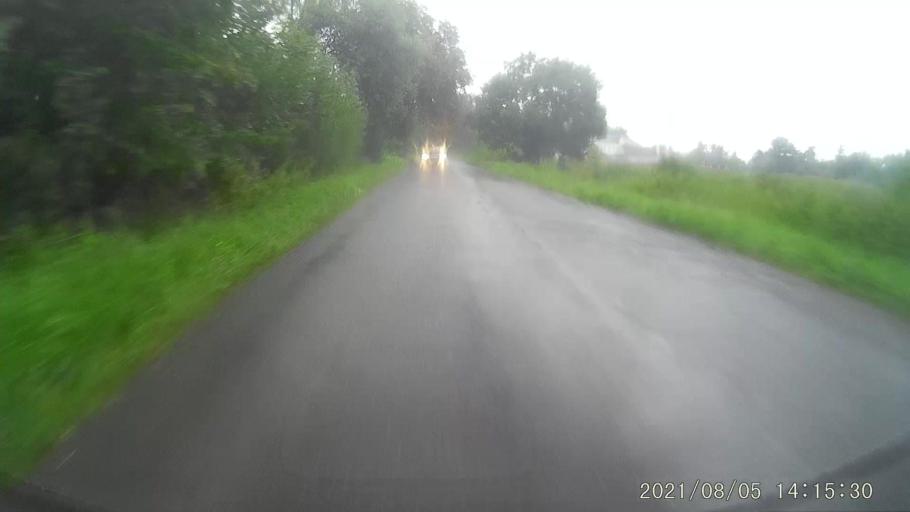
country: PL
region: Opole Voivodeship
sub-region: Powiat prudnicki
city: Biala
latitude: 50.4633
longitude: 17.7335
